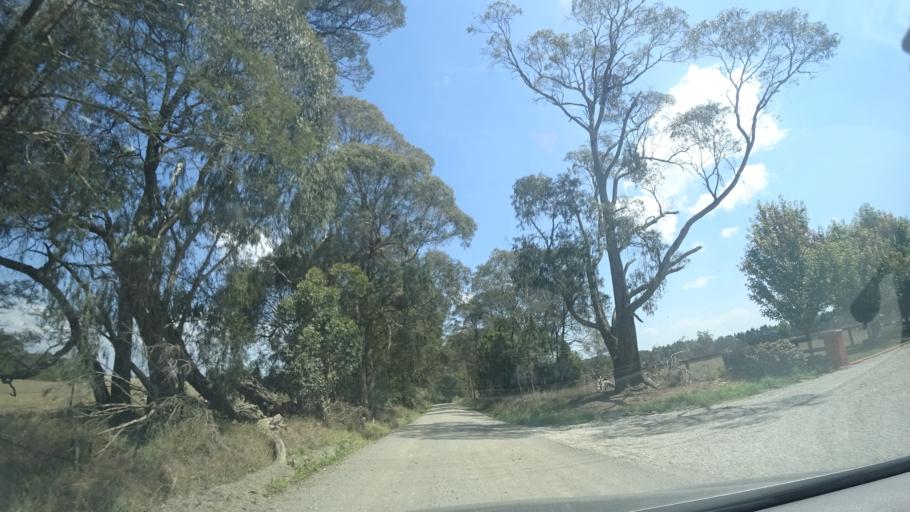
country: AU
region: New South Wales
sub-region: Wingecarribee
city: Bundanoon
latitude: -34.6219
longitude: 150.2700
